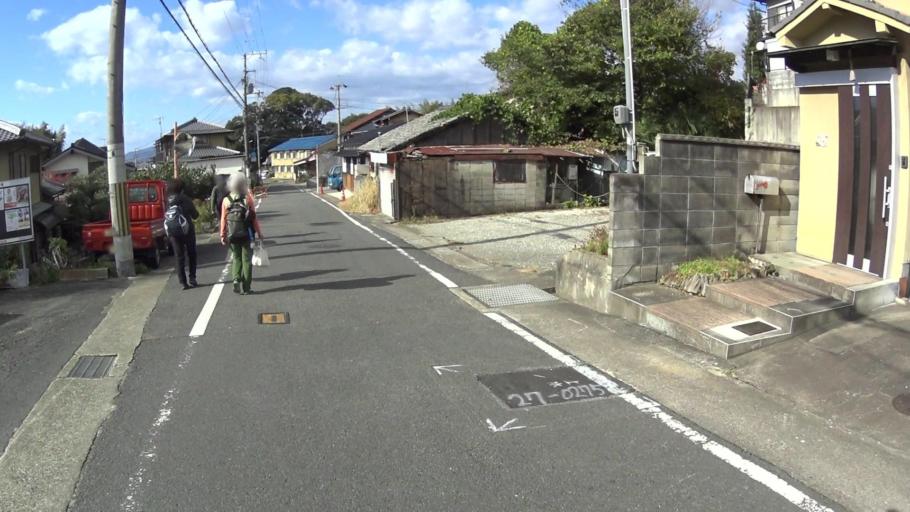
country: JP
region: Kyoto
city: Uji
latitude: 34.9543
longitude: 135.7827
